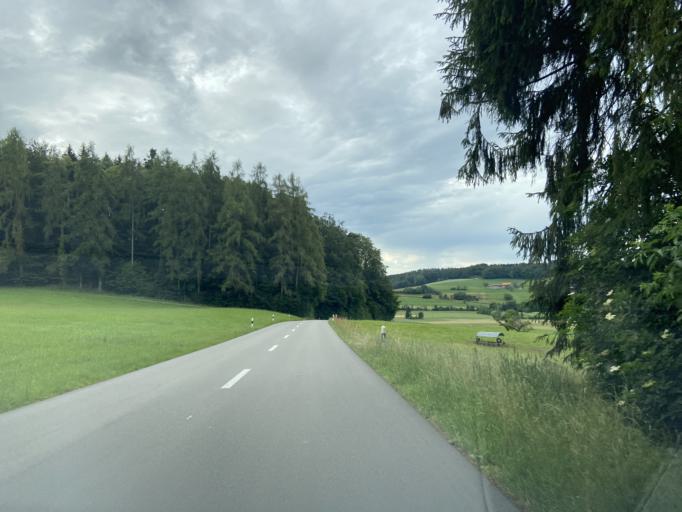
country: CH
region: Thurgau
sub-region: Muenchwilen District
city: Aadorf
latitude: 47.4670
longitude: 8.8914
